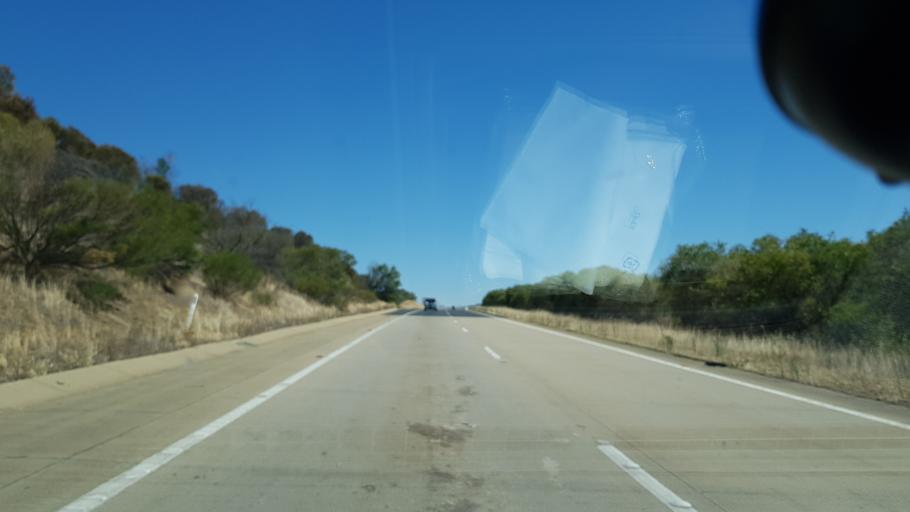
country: AU
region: New South Wales
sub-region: Gundagai
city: Gundagai
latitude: -34.8200
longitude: 148.3713
